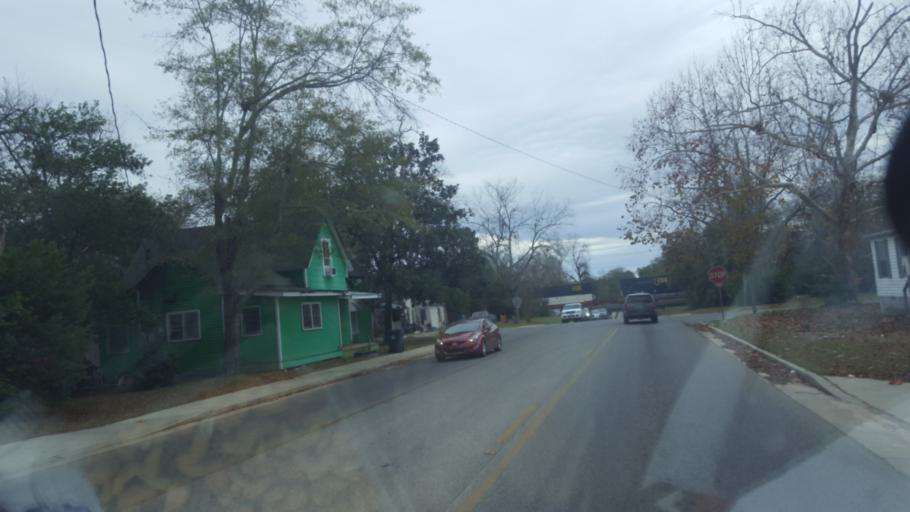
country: US
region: Georgia
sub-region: Ben Hill County
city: Fitzgerald
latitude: 31.7177
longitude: -83.2599
